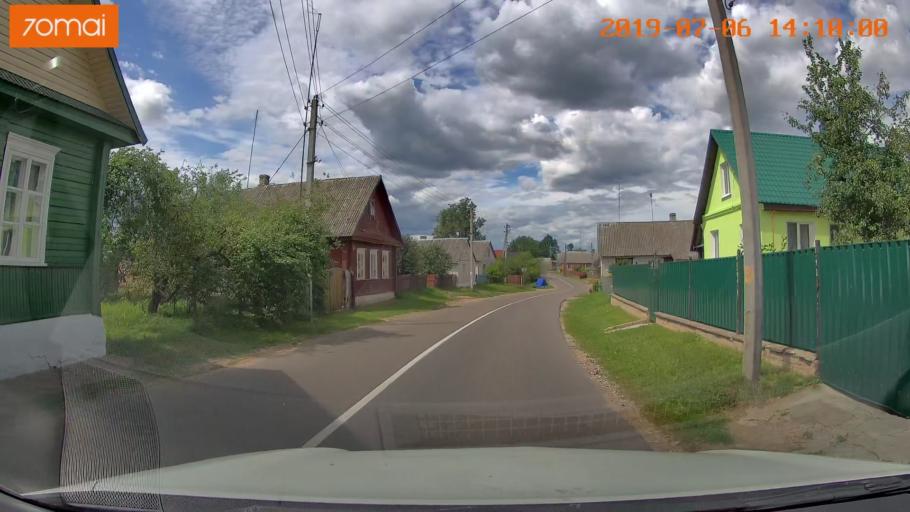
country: BY
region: Minsk
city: Ivyanyets
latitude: 53.8838
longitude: 26.7461
